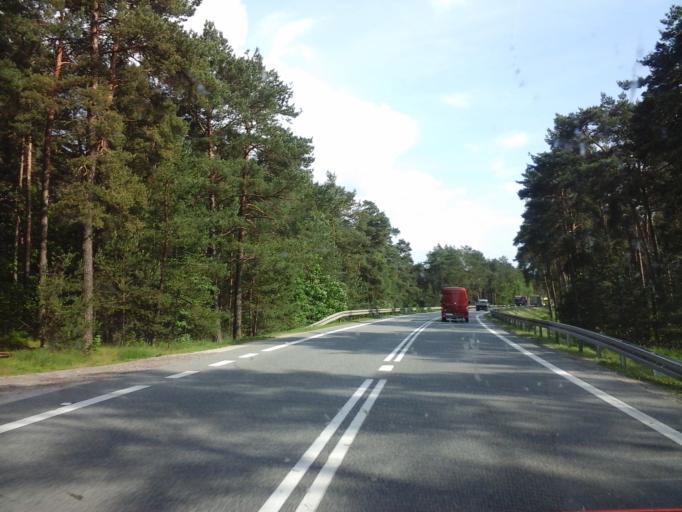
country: PL
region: Swietokrzyskie
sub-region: Powiat konecki
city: Ruda Maleniecka
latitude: 51.1851
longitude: 20.2179
